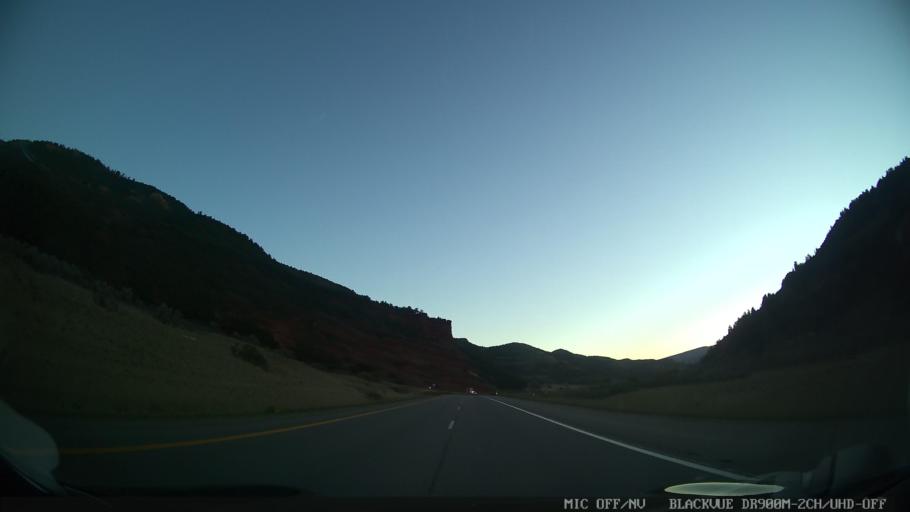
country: US
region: Colorado
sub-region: Eagle County
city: Eagle
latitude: 39.7026
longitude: -106.7304
